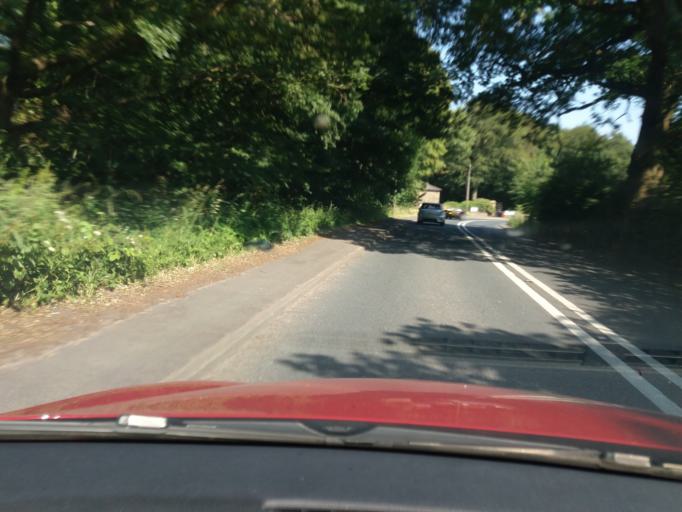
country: GB
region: England
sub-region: Lancashire
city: Clayton-le-Woods
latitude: 53.6841
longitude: -2.6509
